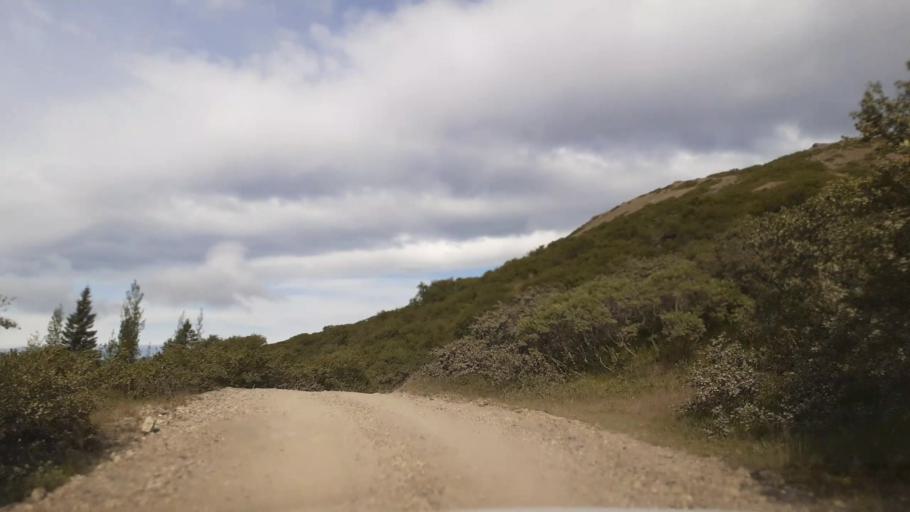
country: IS
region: East
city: Hoefn
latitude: 64.4390
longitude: -14.9150
